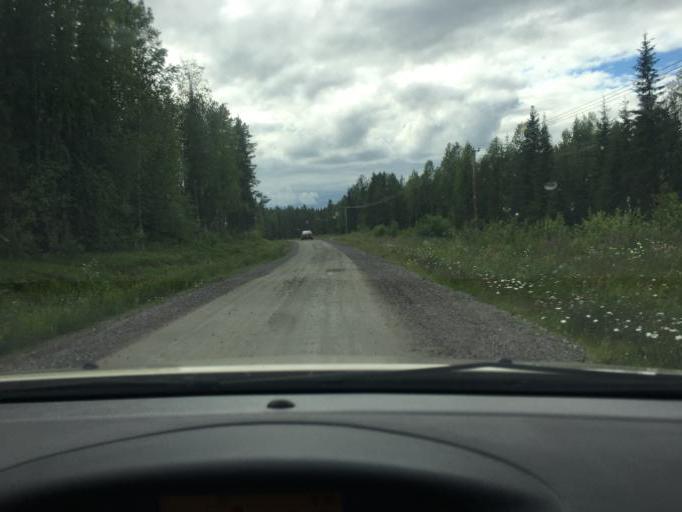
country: SE
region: Norrbotten
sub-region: Overkalix Kommun
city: OEverkalix
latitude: 66.0893
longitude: 22.8462
